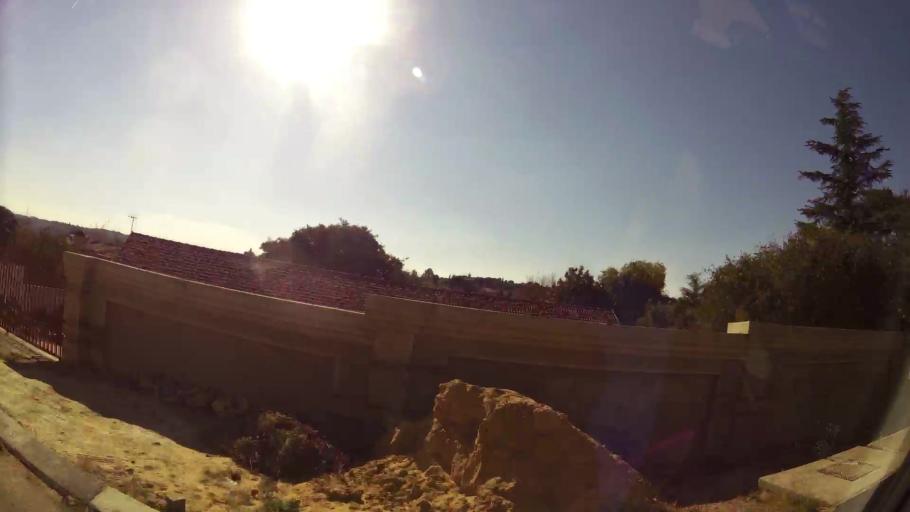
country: ZA
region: Gauteng
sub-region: City of Johannesburg Metropolitan Municipality
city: Johannesburg
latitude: -26.2785
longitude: 28.0174
